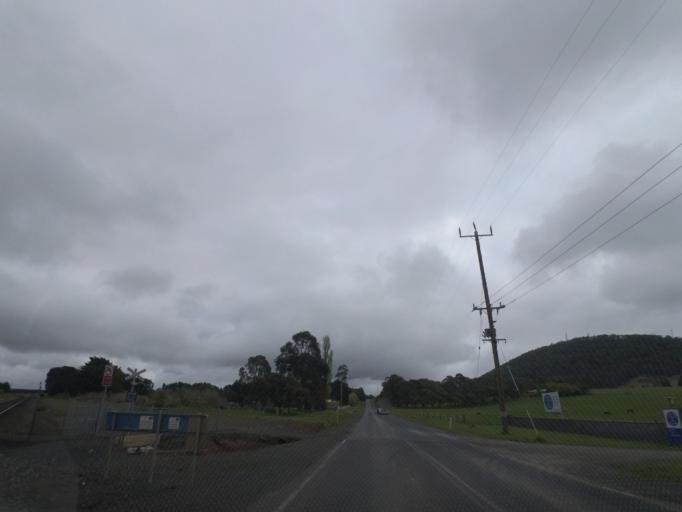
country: AU
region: Victoria
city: Brown Hill
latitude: -37.5883
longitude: 143.9628
